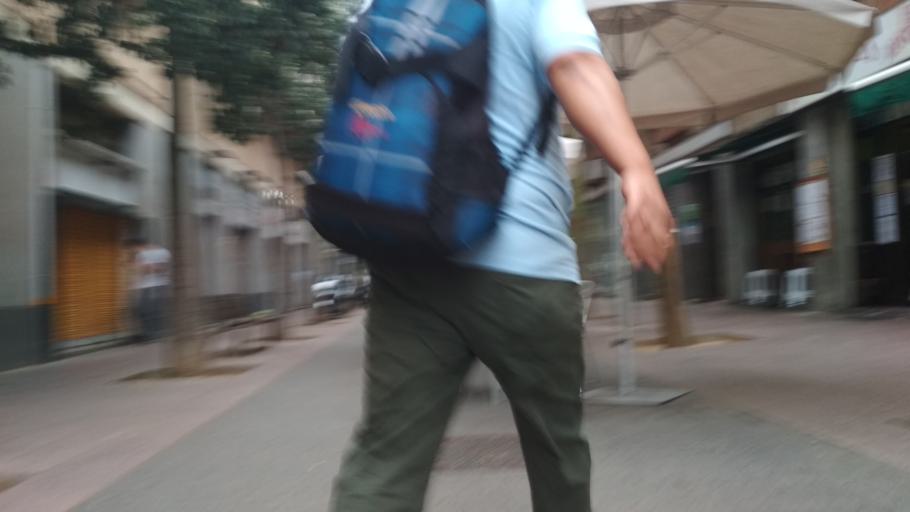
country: ES
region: Catalonia
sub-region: Provincia de Barcelona
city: Sant Andreu de Palomar
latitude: 41.4296
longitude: 2.1817
